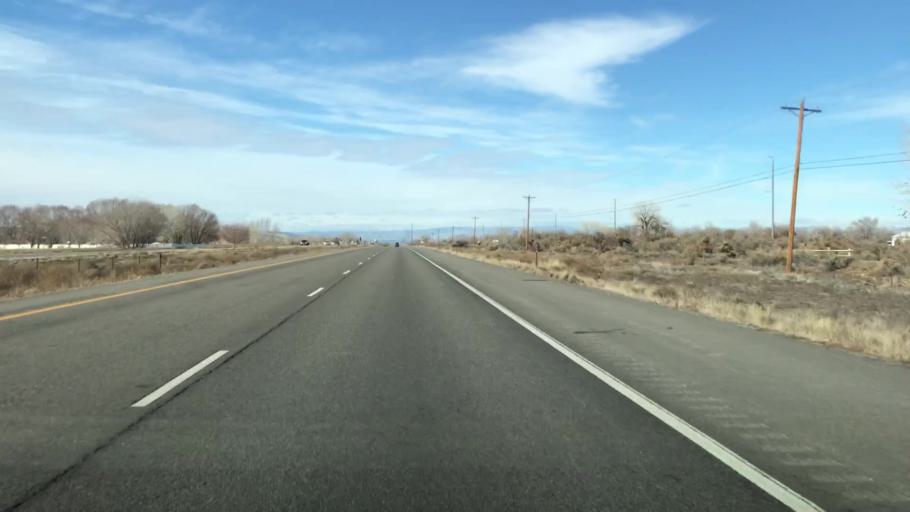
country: US
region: Colorado
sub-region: Mesa County
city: Fruita
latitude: 39.1330
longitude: -108.6918
